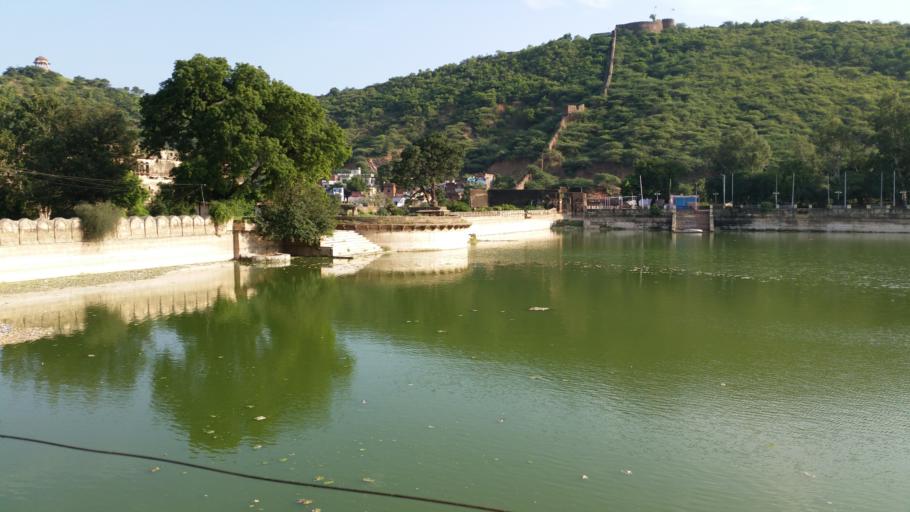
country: IN
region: Rajasthan
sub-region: Bundi
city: Bundi
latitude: 25.4472
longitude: 75.6344
